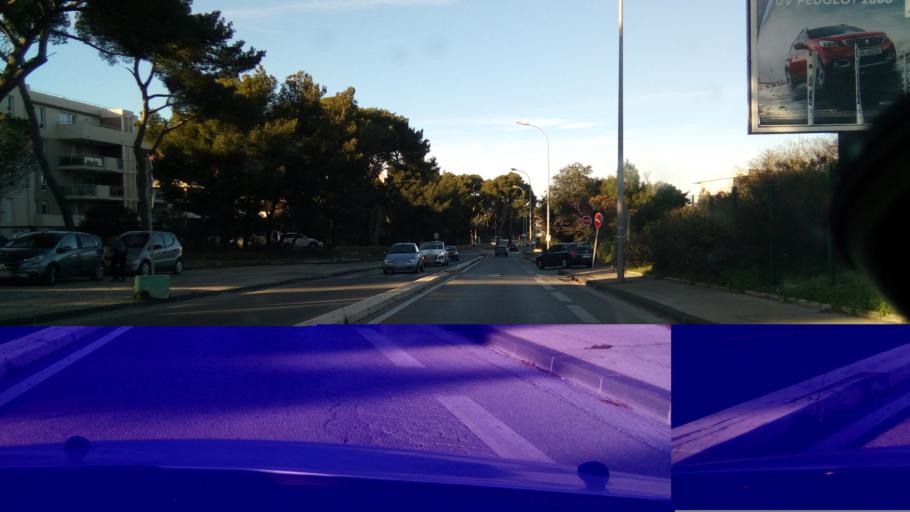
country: FR
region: Provence-Alpes-Cote d'Azur
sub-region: Departement des Bouches-du-Rhone
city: Marseille 09
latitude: 43.2330
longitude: 5.4000
